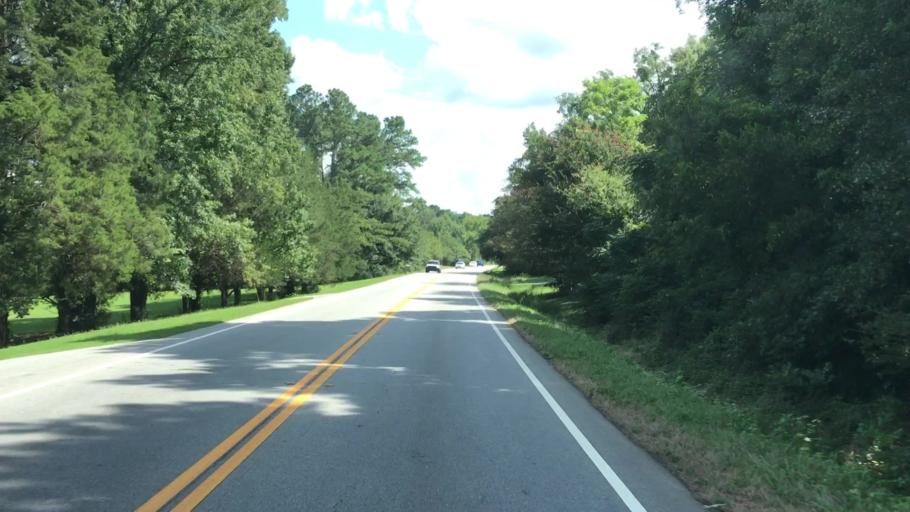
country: US
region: Georgia
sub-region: Newton County
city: Oxford
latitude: 33.6738
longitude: -83.8506
